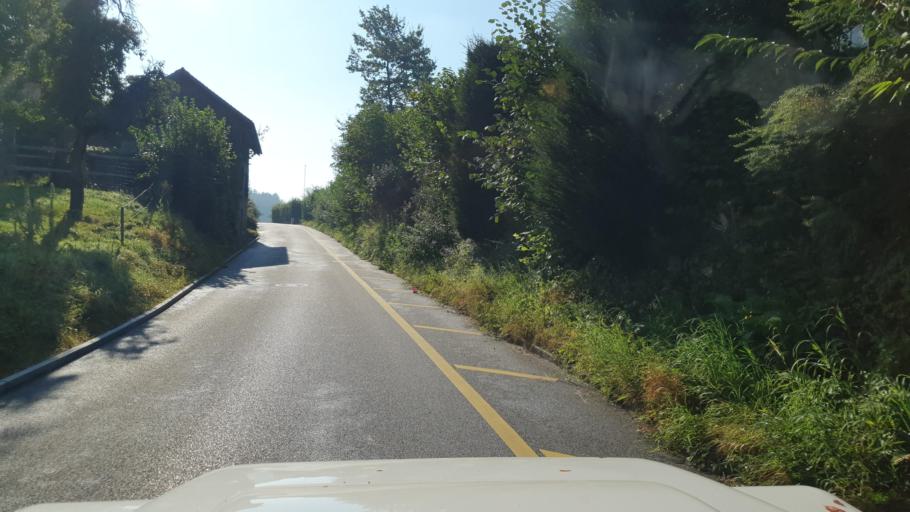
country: CH
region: Aargau
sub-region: Bezirk Bremgarten
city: Villmergen
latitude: 47.3419
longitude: 8.2473
